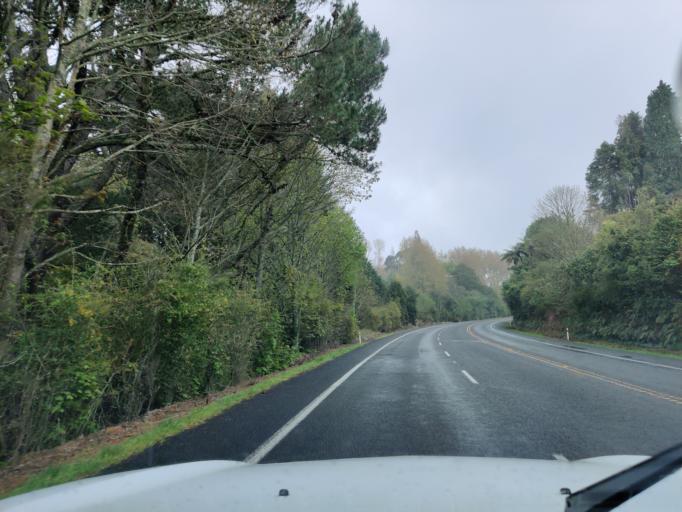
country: NZ
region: Bay of Plenty
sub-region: Rotorua District
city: Rotorua
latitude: -38.0756
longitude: 176.1631
